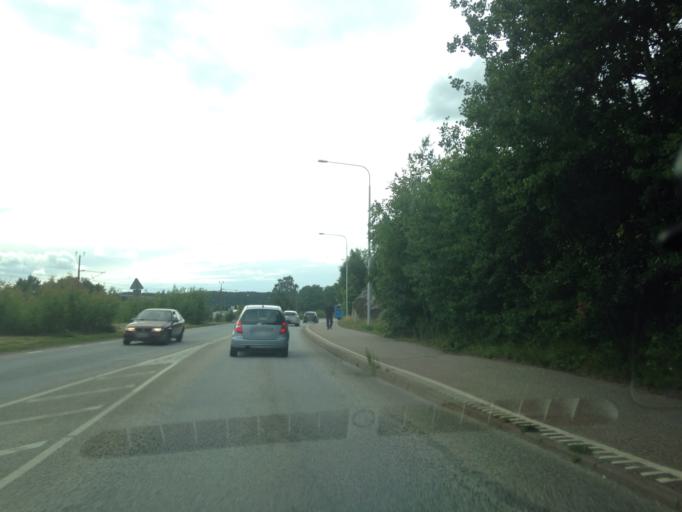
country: SE
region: Vaestra Goetaland
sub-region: Goteborg
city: Goeteborg
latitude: 57.7279
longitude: 11.9627
